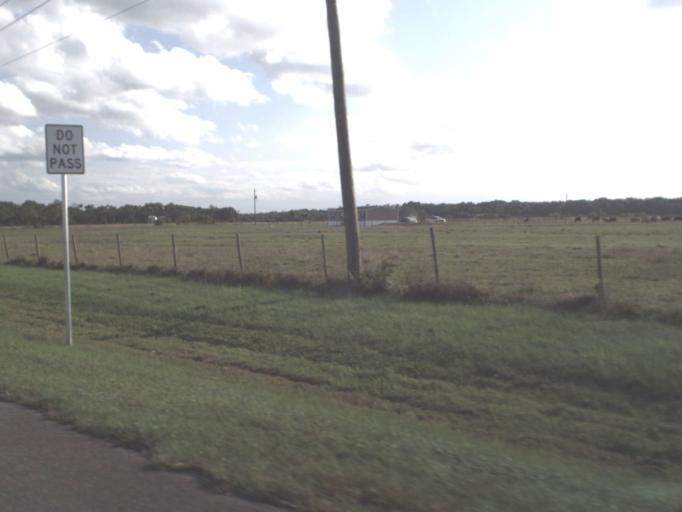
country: US
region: Florida
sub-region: Flagler County
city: Bunnell
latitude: 29.3232
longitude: -81.3104
